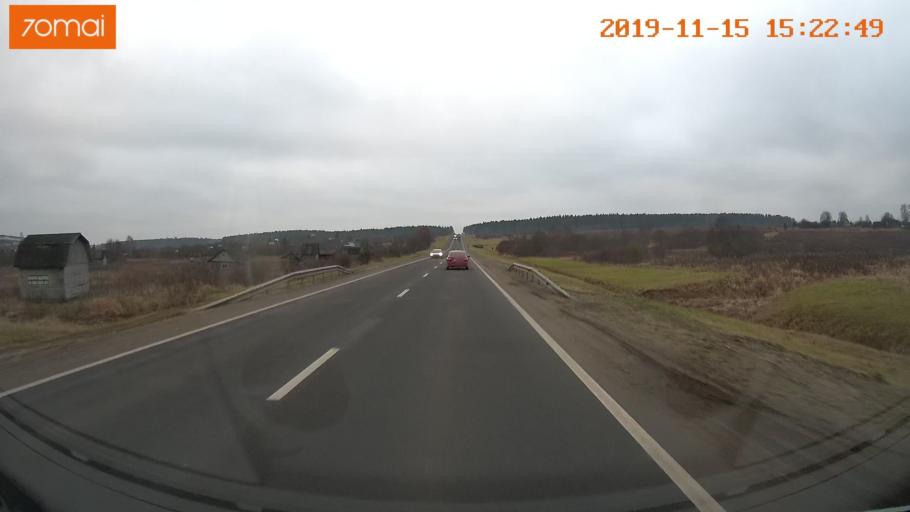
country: RU
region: Jaroslavl
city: Danilov
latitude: 58.1983
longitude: 40.1315
